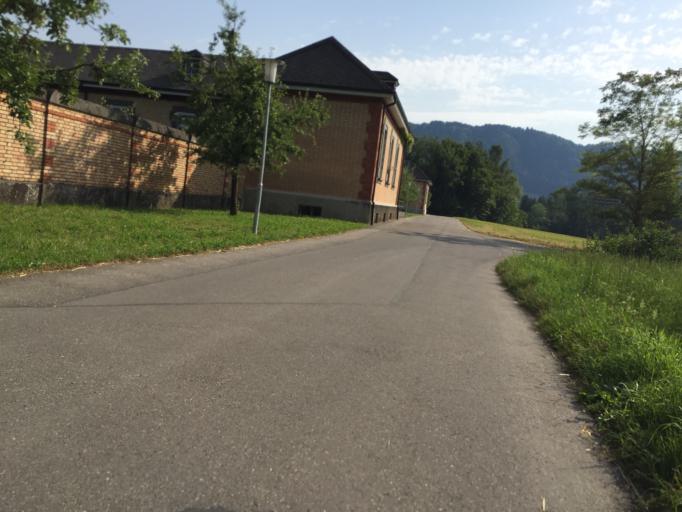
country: CH
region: Bern
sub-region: Bern-Mittelland District
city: Munsingen
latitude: 46.8820
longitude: 7.5507
